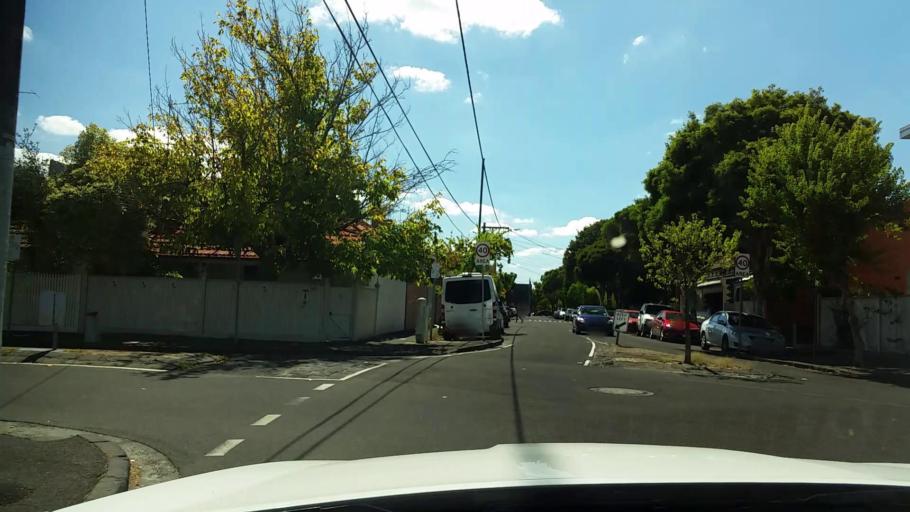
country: AU
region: Victoria
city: Windsor
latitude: -37.8528
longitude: 144.9884
